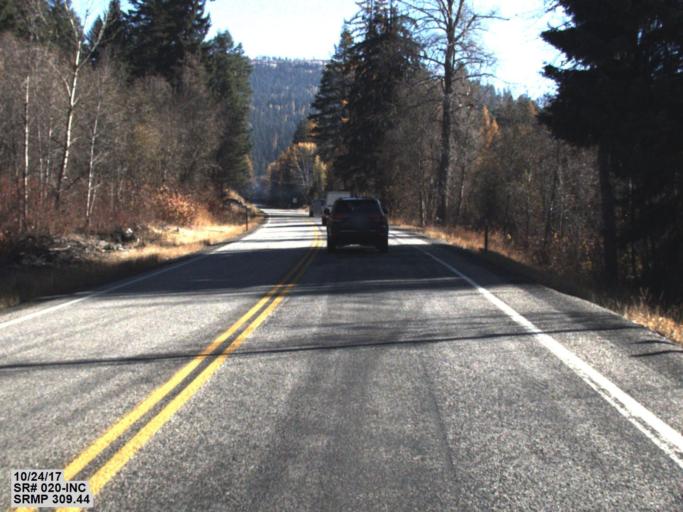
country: US
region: Washington
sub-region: Ferry County
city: Republic
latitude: 48.5978
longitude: -118.6476
